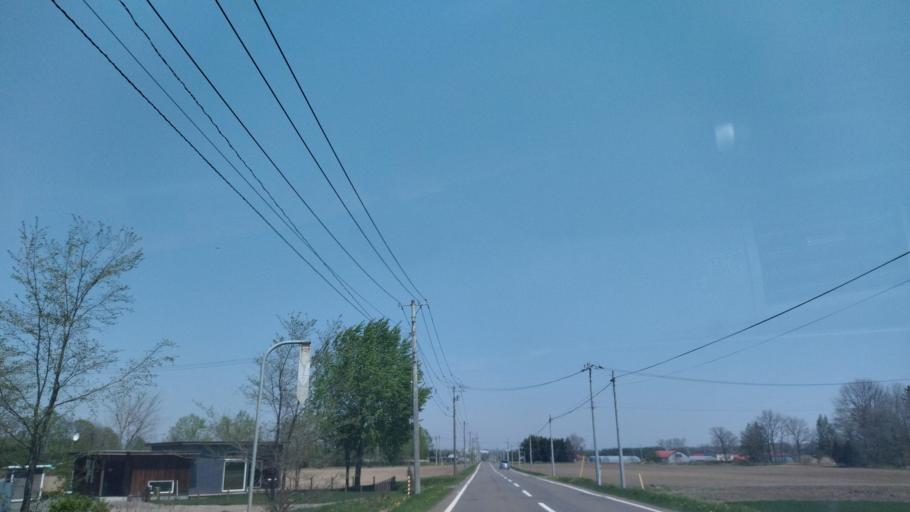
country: JP
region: Hokkaido
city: Obihiro
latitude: 42.8863
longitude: 143.0231
